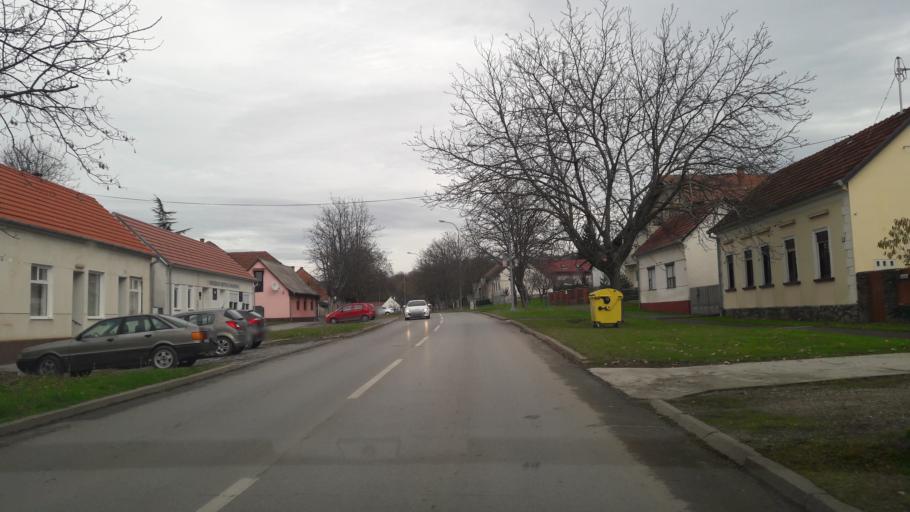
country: HR
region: Virovitick-Podravska
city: Orahovica
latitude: 45.5311
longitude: 17.8846
